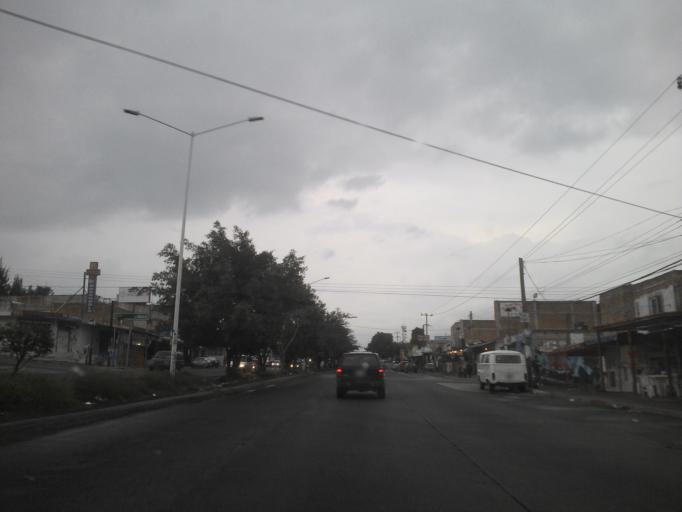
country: MX
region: Jalisco
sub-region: Tlajomulco de Zuniga
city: Altus Bosques
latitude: 20.6091
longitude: -103.3765
